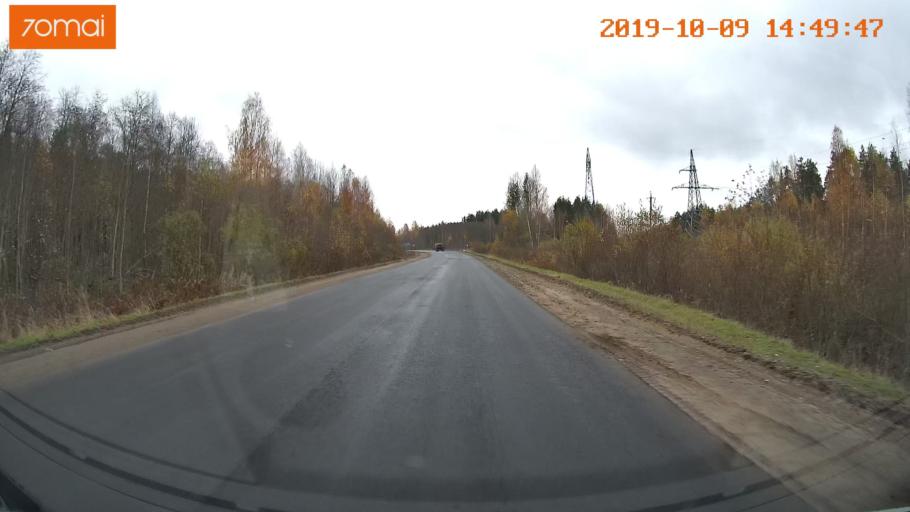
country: RU
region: Kostroma
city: Chistyye Bory
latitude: 58.3899
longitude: 41.5876
